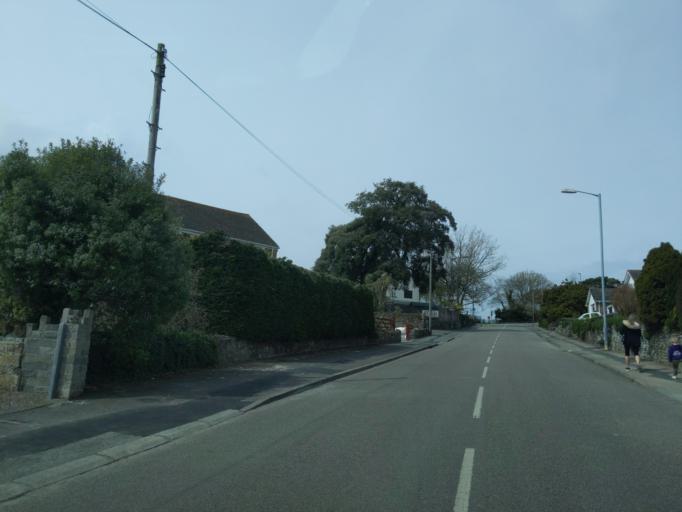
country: GB
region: England
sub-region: Cornwall
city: Torpoint
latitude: 50.3746
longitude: -4.2069
